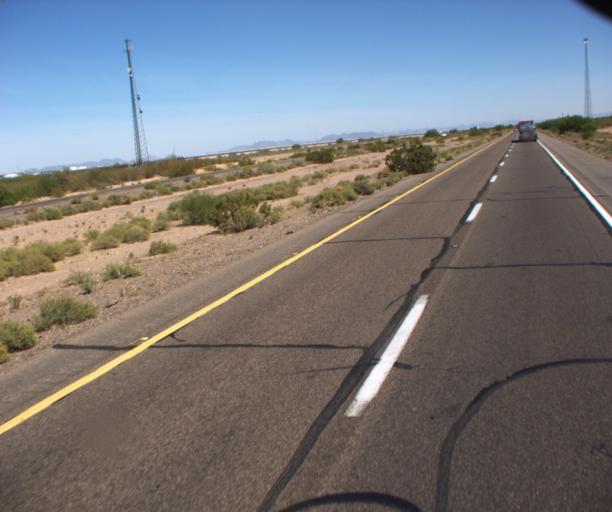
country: US
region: Arizona
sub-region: Maricopa County
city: Gila Bend
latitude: 32.9049
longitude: -112.9903
